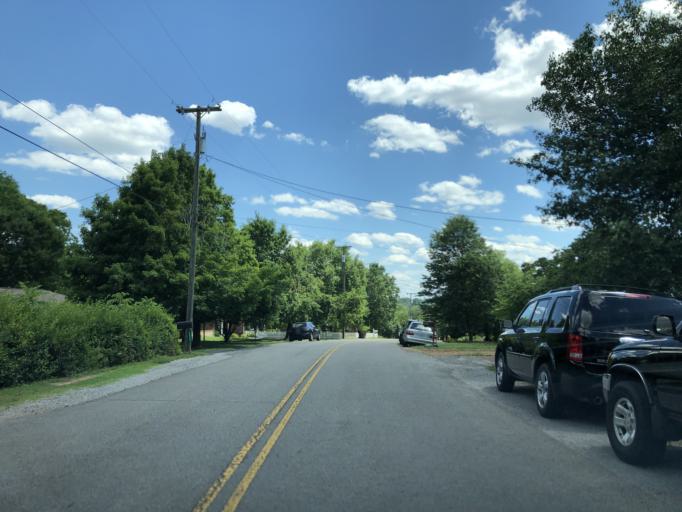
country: US
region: Tennessee
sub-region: Davidson County
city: Nashville
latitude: 36.1777
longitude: -86.7192
